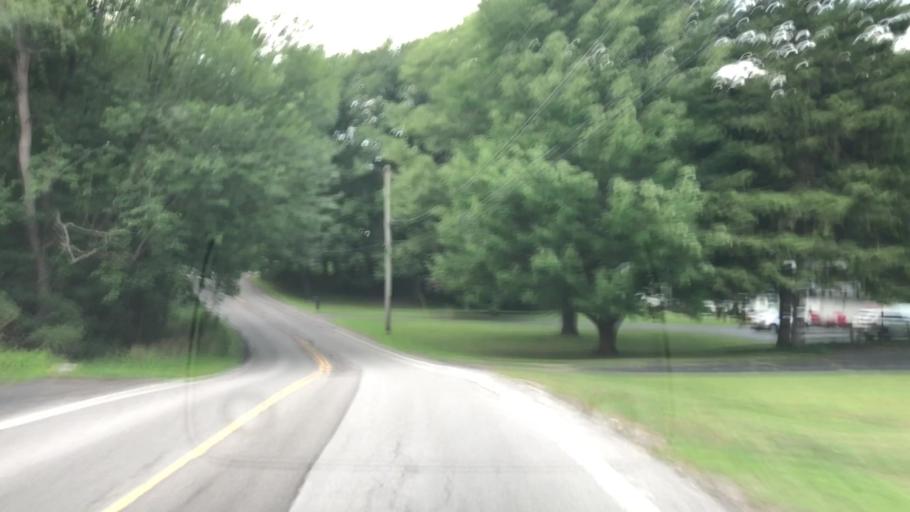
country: US
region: New York
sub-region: Erie County
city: East Aurora
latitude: 42.7810
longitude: -78.6032
